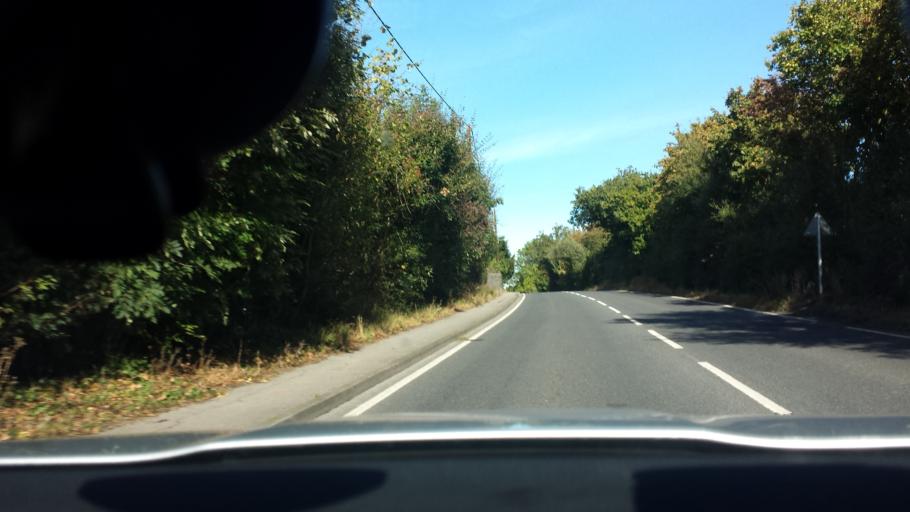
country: GB
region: England
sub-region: Kent
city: Staplehurst
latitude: 51.1736
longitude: 0.5526
